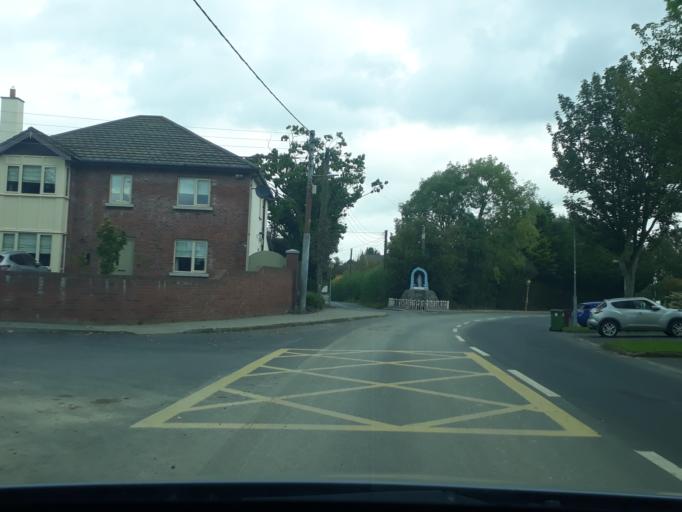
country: IE
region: Leinster
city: Lucan
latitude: 53.3501
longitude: -6.4646
